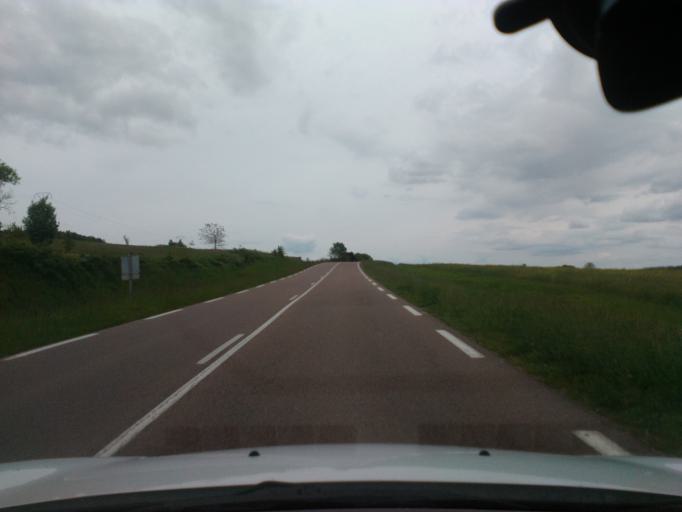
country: FR
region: Champagne-Ardenne
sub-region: Departement de l'Aube
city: Bar-sur-Aube
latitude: 48.2571
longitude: 4.6776
